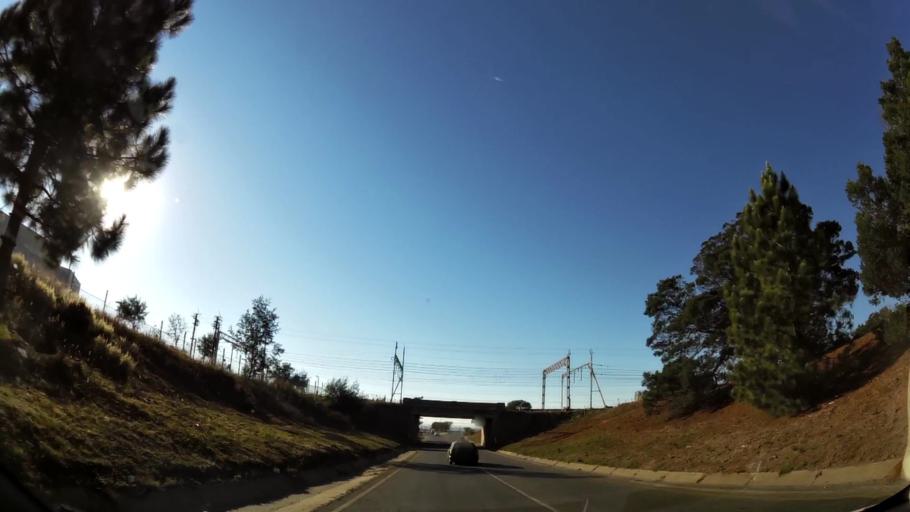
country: ZA
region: Gauteng
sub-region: Ekurhuleni Metropolitan Municipality
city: Tembisa
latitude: -26.0397
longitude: 28.2534
